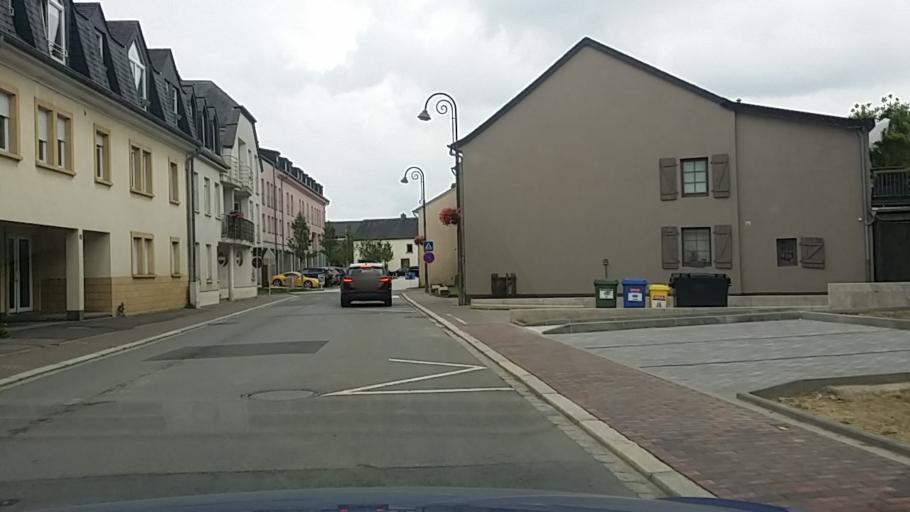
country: LU
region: Luxembourg
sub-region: Canton de Luxembourg
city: Bertrange
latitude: 49.6121
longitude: 6.0486
